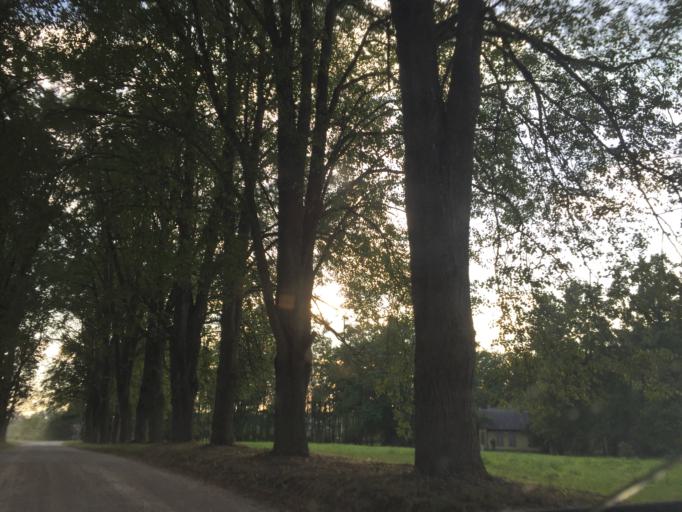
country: LV
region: Lecava
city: Iecava
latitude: 56.5910
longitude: 24.2135
